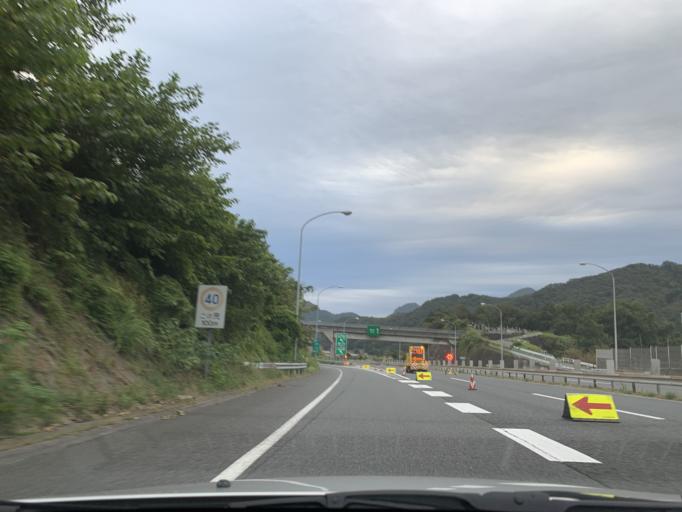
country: JP
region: Yamanashi
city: Otsuki
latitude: 35.6014
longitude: 138.9124
